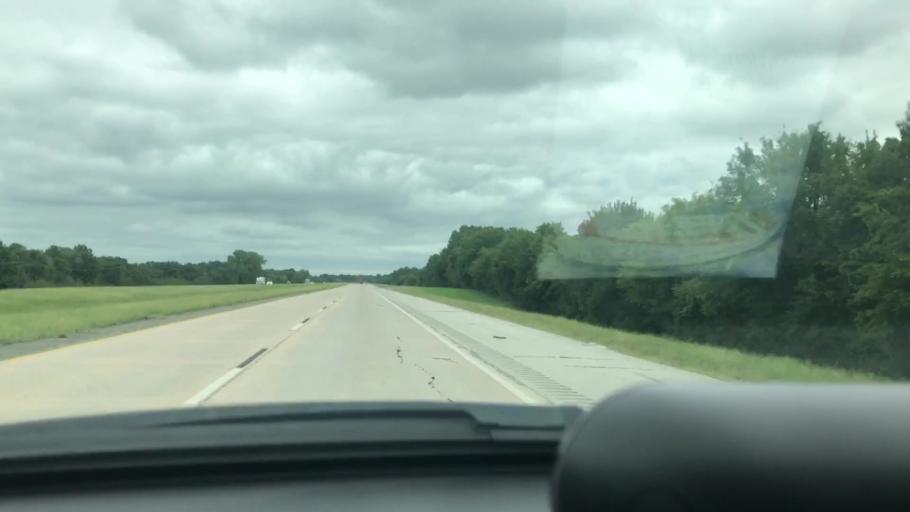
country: US
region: Oklahoma
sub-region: Wagoner County
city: Wagoner
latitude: 35.8954
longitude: -95.4026
